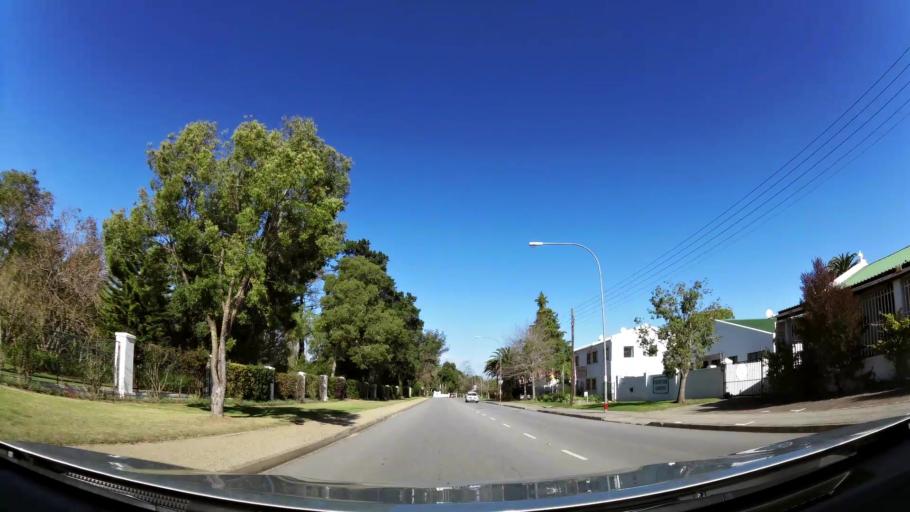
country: ZA
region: Western Cape
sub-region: Eden District Municipality
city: George
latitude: -33.9499
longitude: 22.4075
